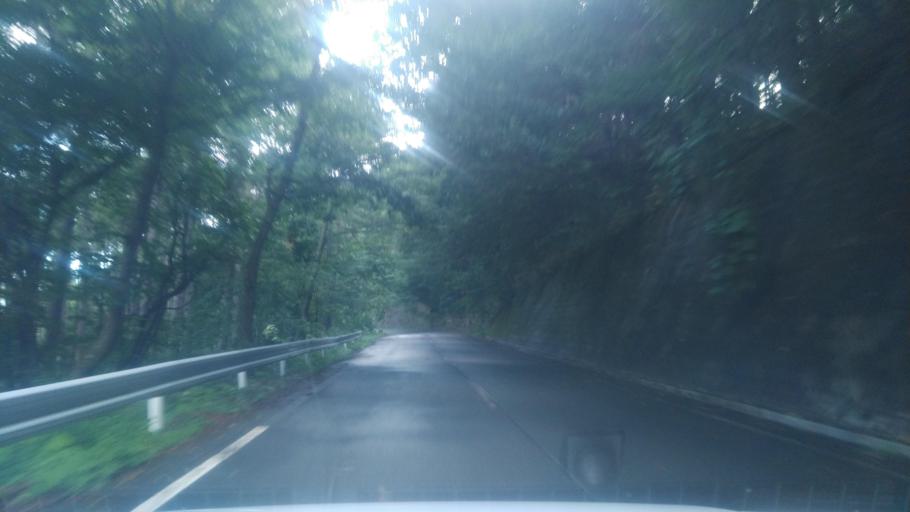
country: JP
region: Nagano
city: Ueda
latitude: 36.5151
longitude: 138.3643
